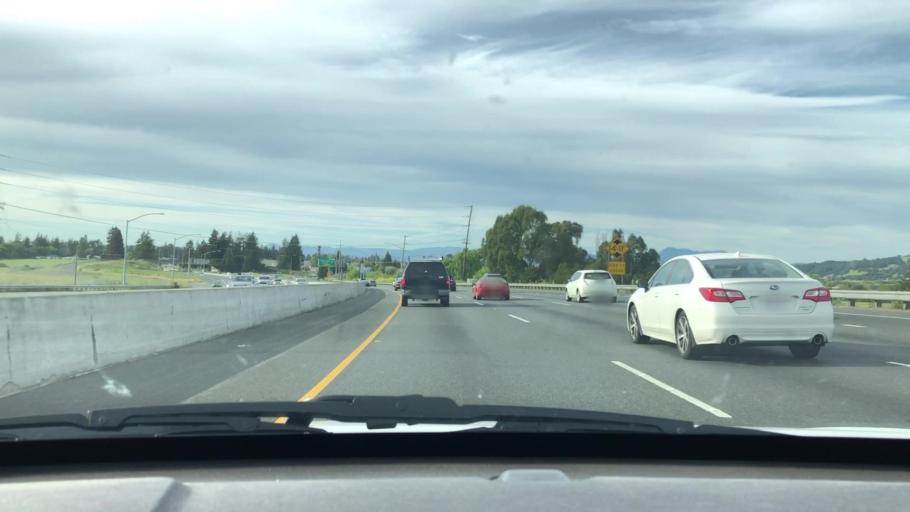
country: US
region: California
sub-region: Sonoma County
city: Rohnert Park
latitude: 38.3671
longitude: -122.7113
